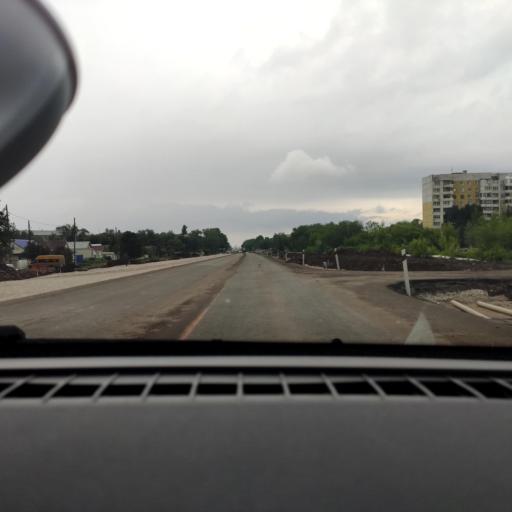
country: RU
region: Samara
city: Samara
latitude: 53.1117
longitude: 50.0827
